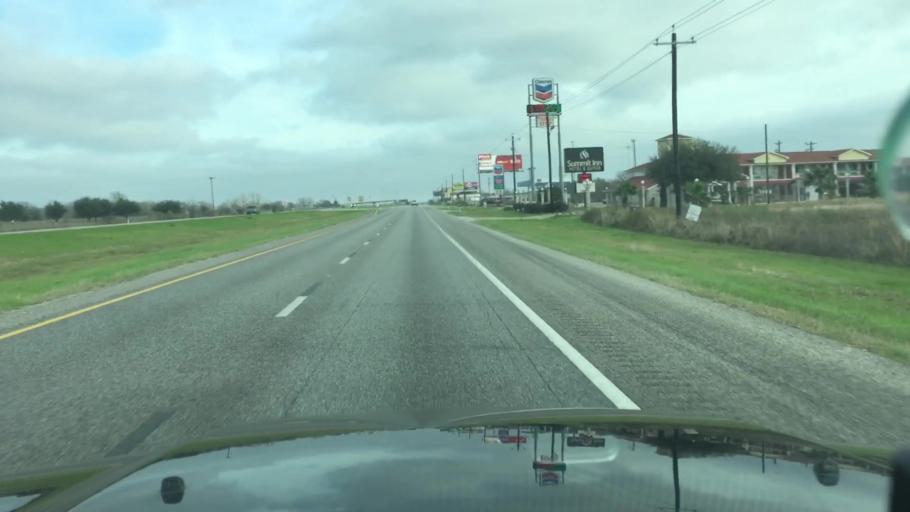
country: US
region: Texas
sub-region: Waller County
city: Hempstead
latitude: 30.1183
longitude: -96.0927
